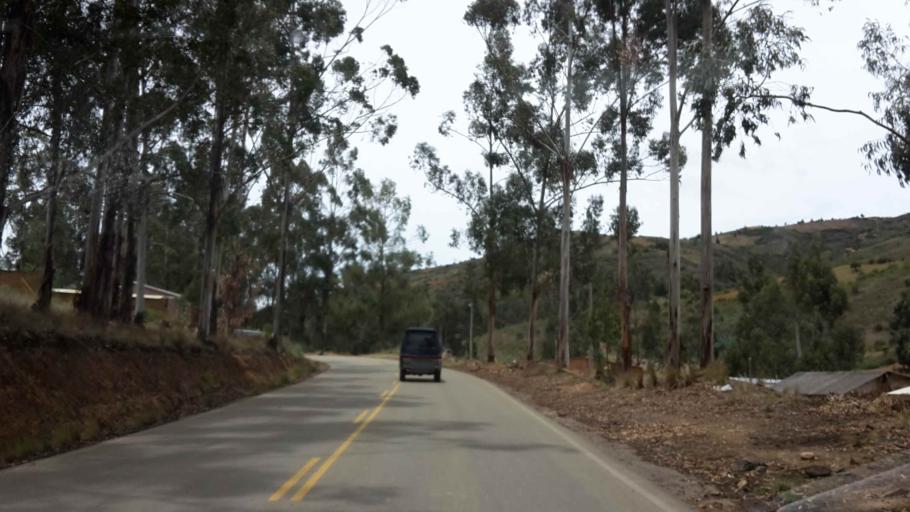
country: BO
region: Cochabamba
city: Totora
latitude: -17.7194
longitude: -65.2042
